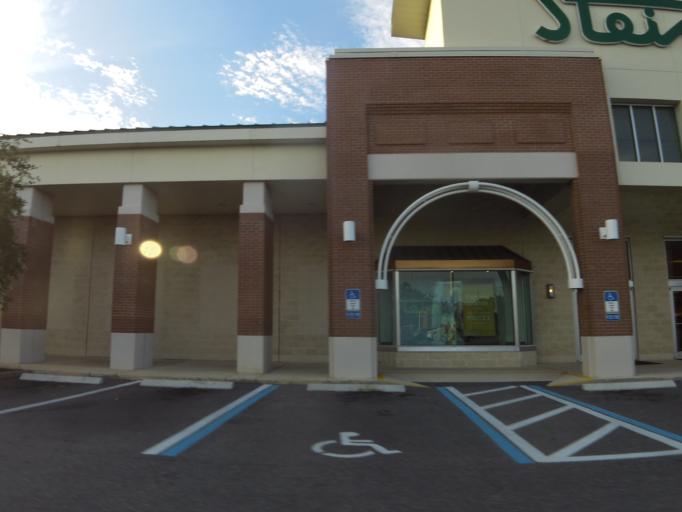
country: US
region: Florida
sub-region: Saint Johns County
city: Ponte Vedra Beach
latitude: 30.2172
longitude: -81.5176
